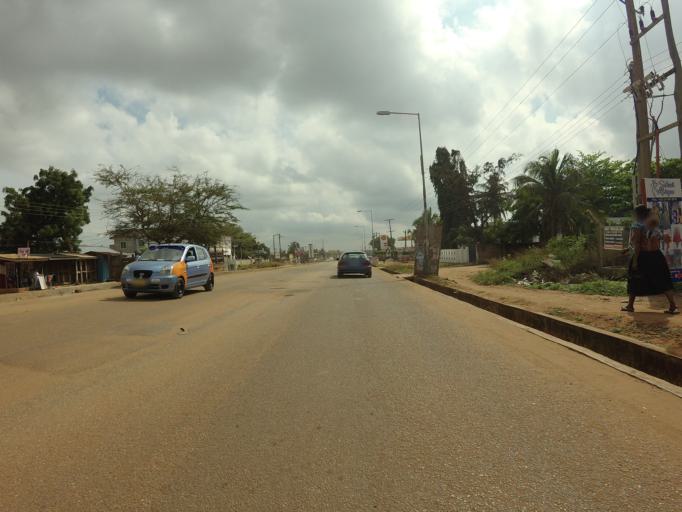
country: GH
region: Greater Accra
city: Teshi Old Town
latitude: 5.6091
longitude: -0.1087
